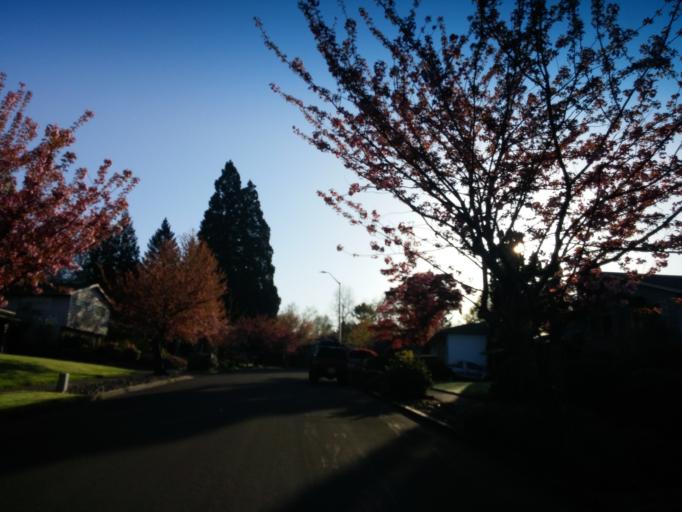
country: US
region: Oregon
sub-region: Washington County
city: Cedar Hills
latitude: 45.5052
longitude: -122.7879
